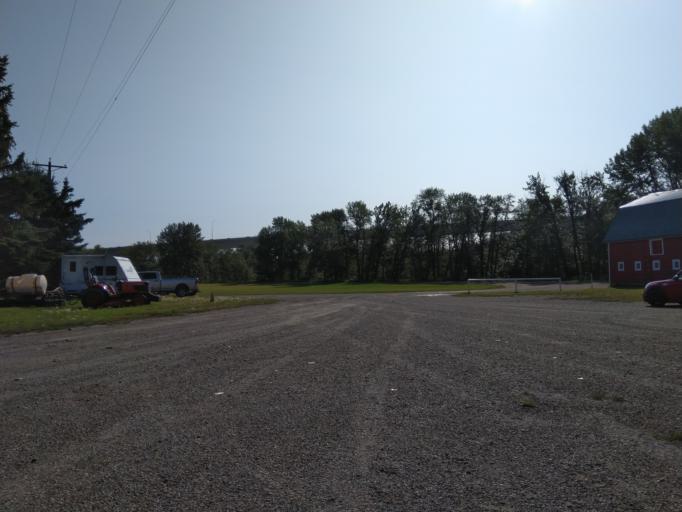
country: CA
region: Alberta
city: Calgary
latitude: 51.0985
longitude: -114.2374
